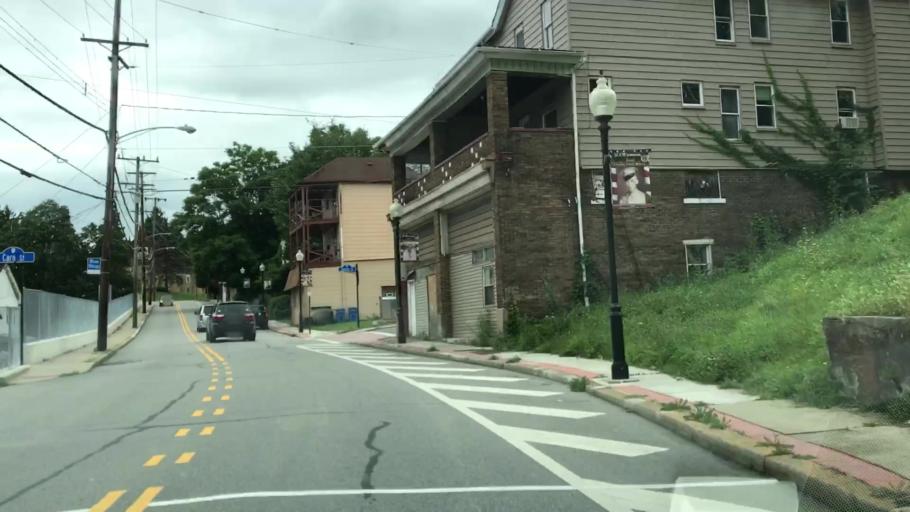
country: US
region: Pennsylvania
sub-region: Allegheny County
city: Heidelberg
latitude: 40.3981
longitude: -80.0883
